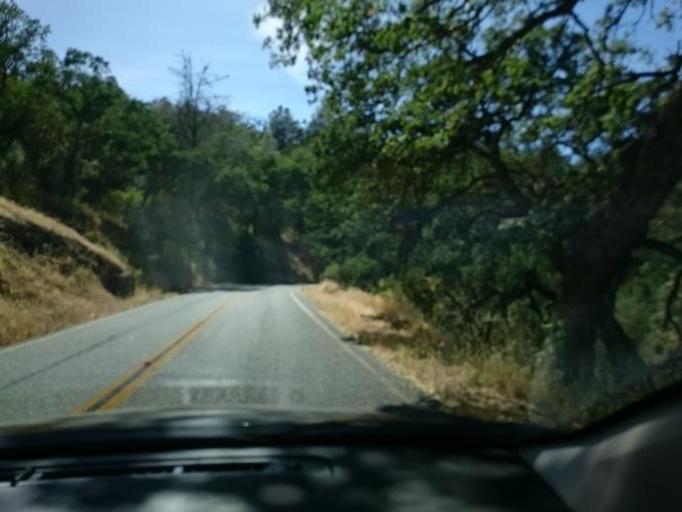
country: US
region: California
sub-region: Santa Clara County
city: East Foothills
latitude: 37.3579
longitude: -121.5814
